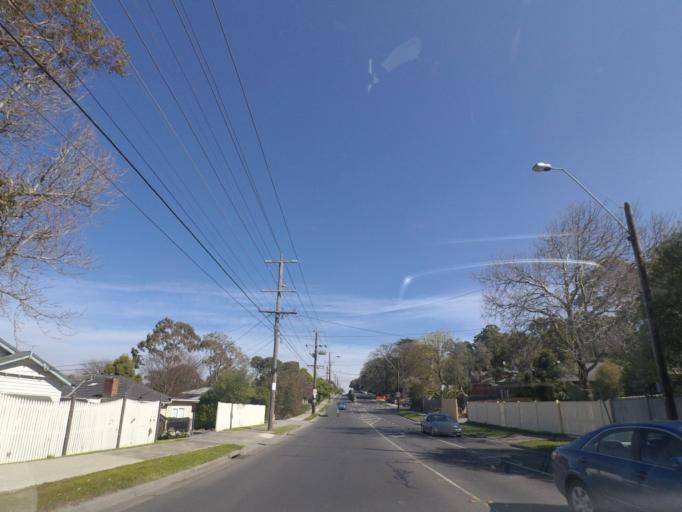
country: AU
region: Victoria
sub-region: Maroondah
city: Ringwood East
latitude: -37.8057
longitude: 145.2270
